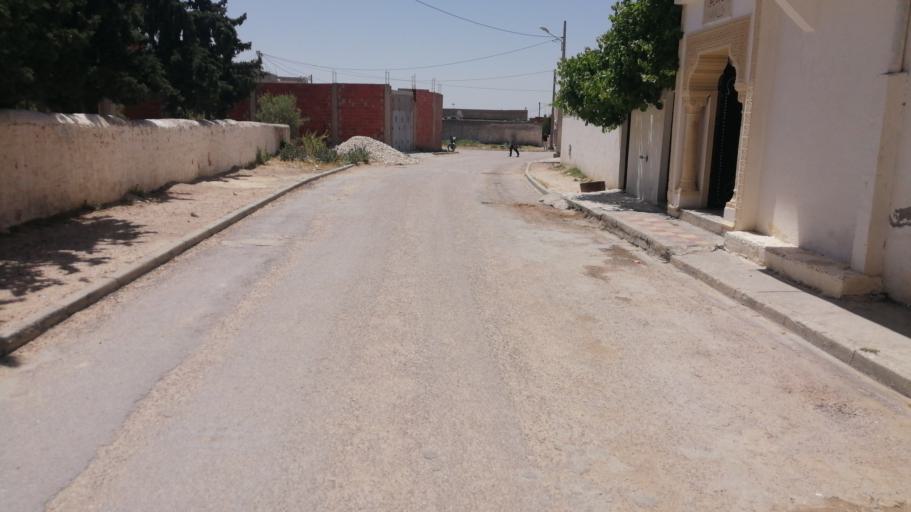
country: TN
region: Silyanah
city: Maktar
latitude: 35.8516
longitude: 9.2037
